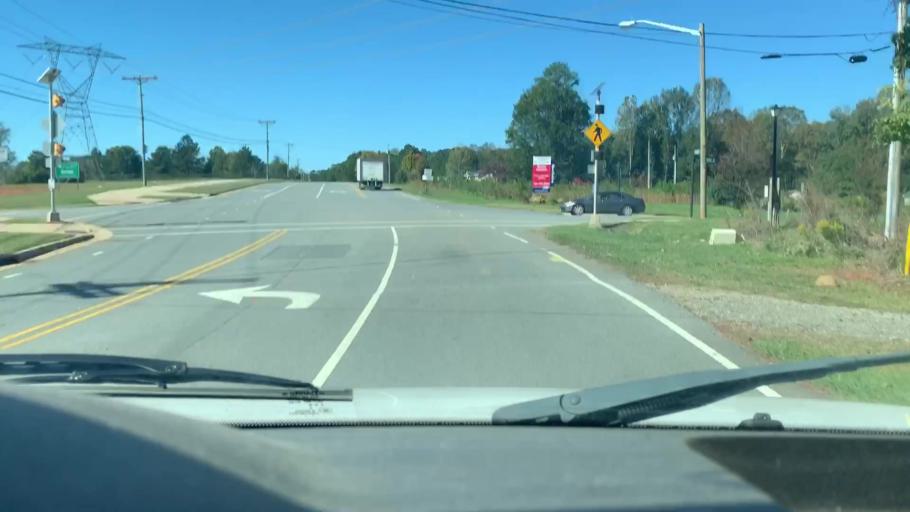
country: US
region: North Carolina
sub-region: Gaston County
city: Davidson
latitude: 35.4697
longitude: -80.8291
